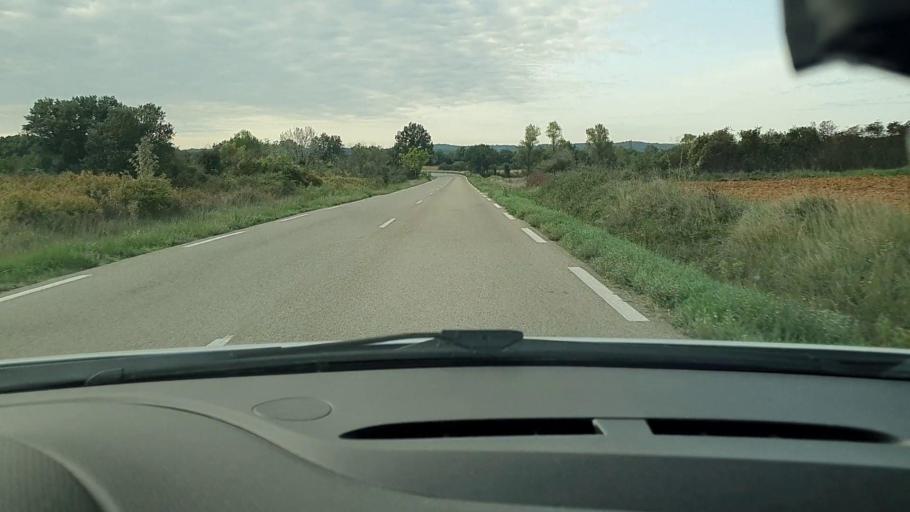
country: FR
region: Languedoc-Roussillon
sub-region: Departement du Gard
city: Mons
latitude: 44.0845
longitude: 4.2182
